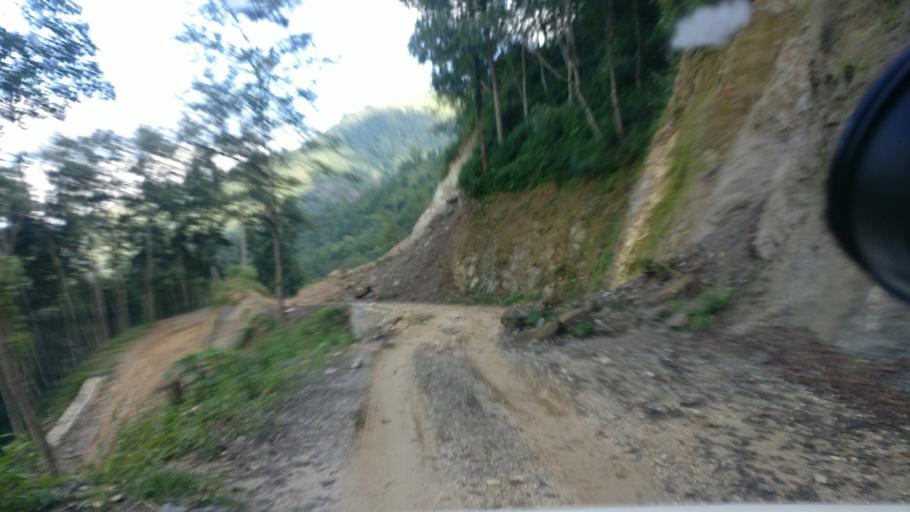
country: NP
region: Western Region
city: Waling
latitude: 28.1166
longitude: 83.6774
